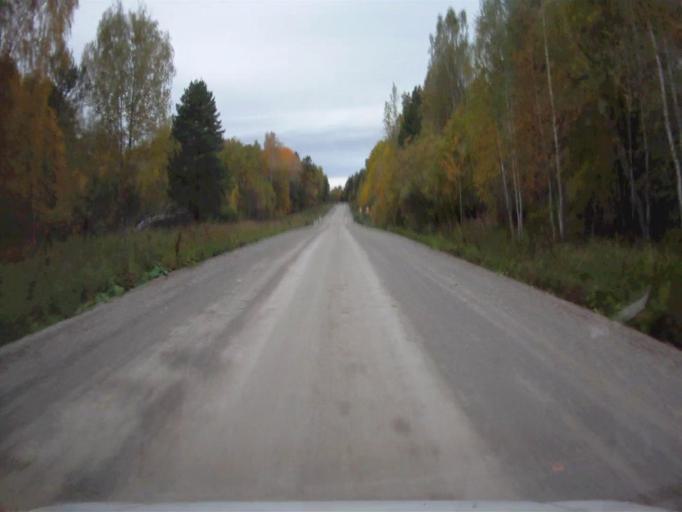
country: RU
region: Chelyabinsk
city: Nyazepetrovsk
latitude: 56.0820
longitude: 59.4218
